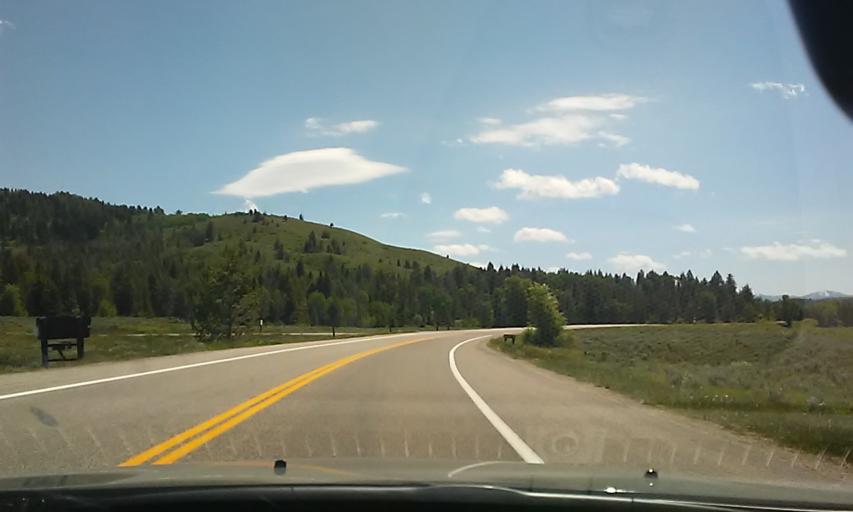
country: US
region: Wyoming
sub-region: Teton County
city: Jackson
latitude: 43.8403
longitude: -110.5078
